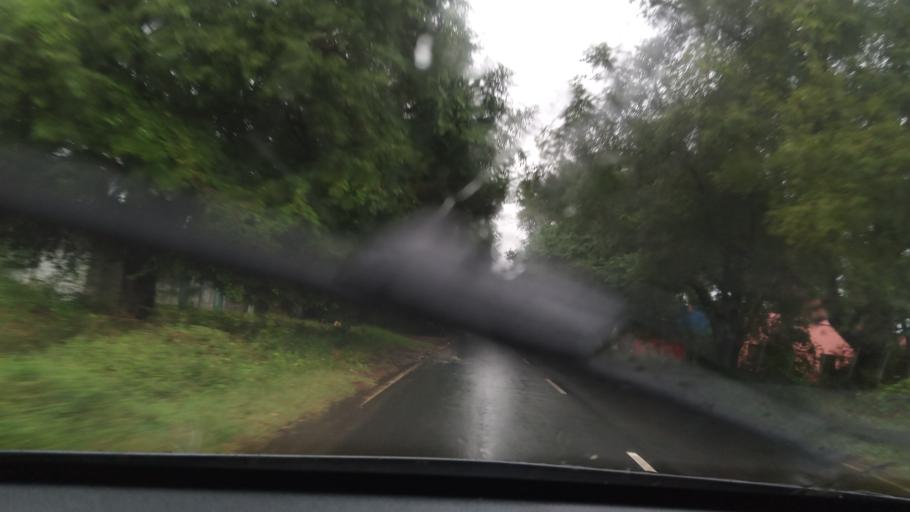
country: IN
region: Tamil Nadu
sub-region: Vellore
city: Kalavai
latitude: 12.8372
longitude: 79.4048
